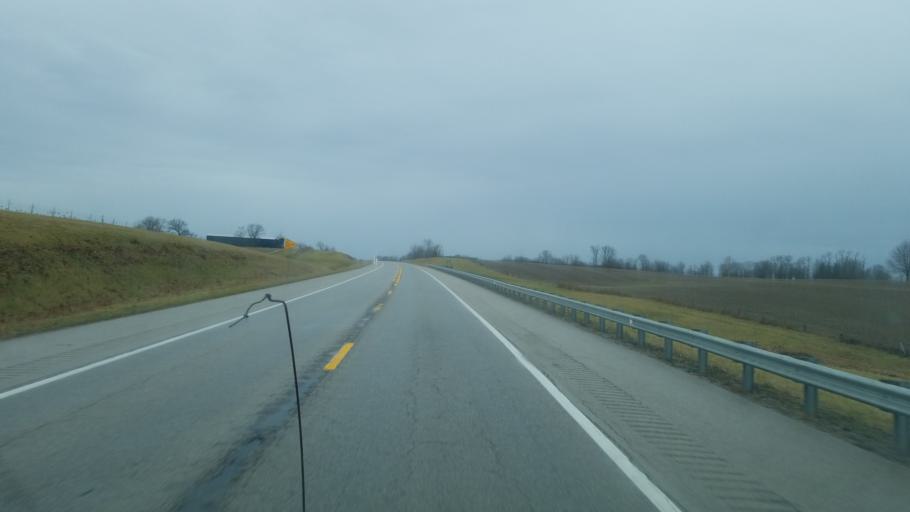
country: US
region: Ohio
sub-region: Adams County
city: Manchester
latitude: 38.5646
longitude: -83.6236
